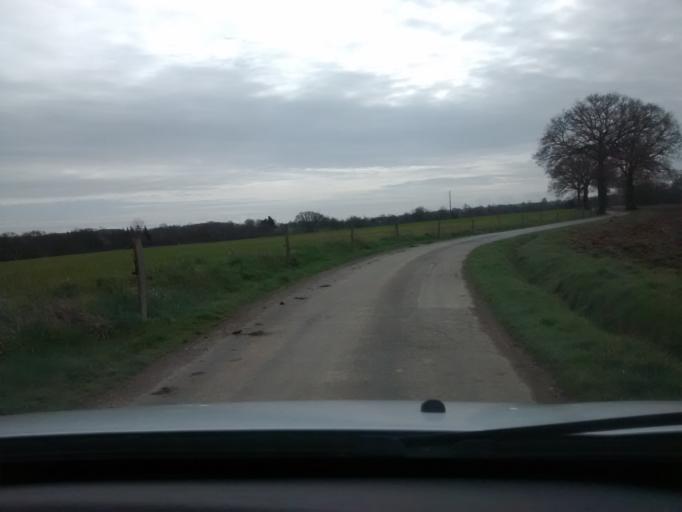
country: FR
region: Brittany
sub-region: Departement d'Ille-et-Vilaine
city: Liffre
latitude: 48.2117
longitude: -1.4780
